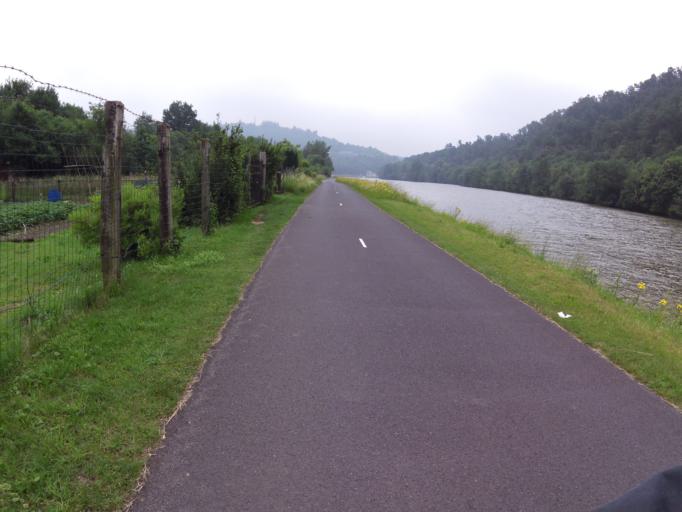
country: FR
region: Champagne-Ardenne
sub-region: Departement des Ardennes
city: Fumay
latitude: 49.9812
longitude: 4.6915
